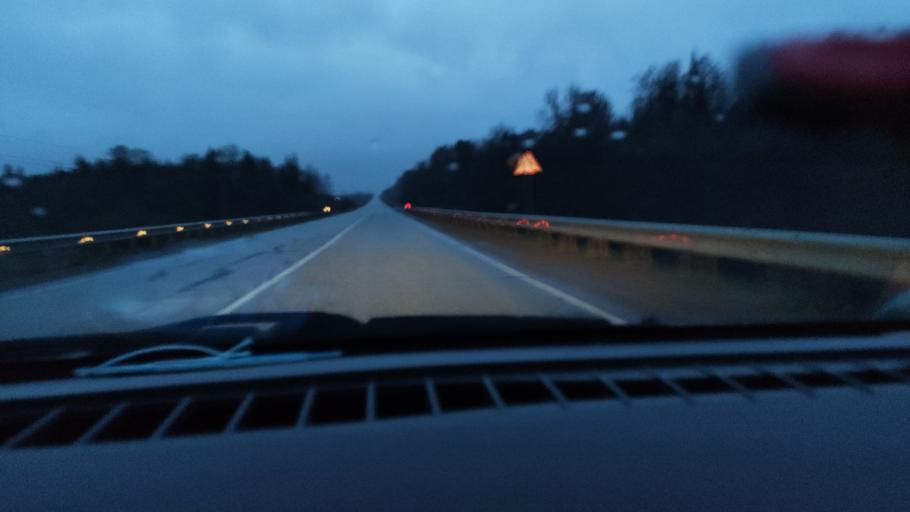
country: RU
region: Udmurtiya
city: Mozhga
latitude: 56.3614
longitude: 52.2594
